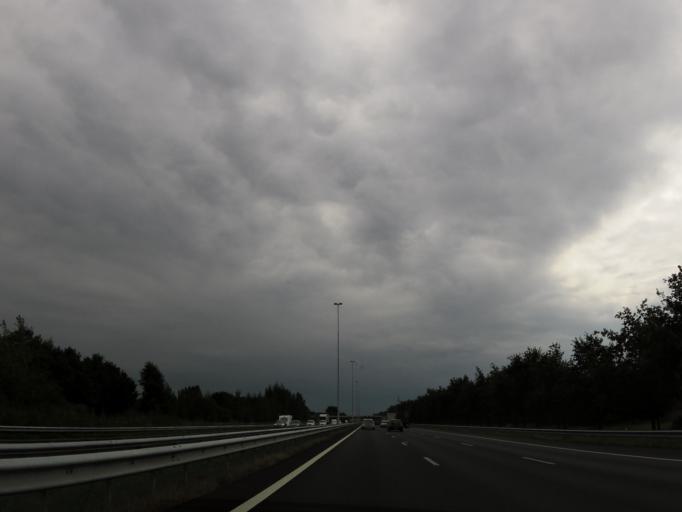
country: NL
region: North Brabant
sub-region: Gemeente Boxtel
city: Boxtel
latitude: 51.5993
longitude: 5.3379
